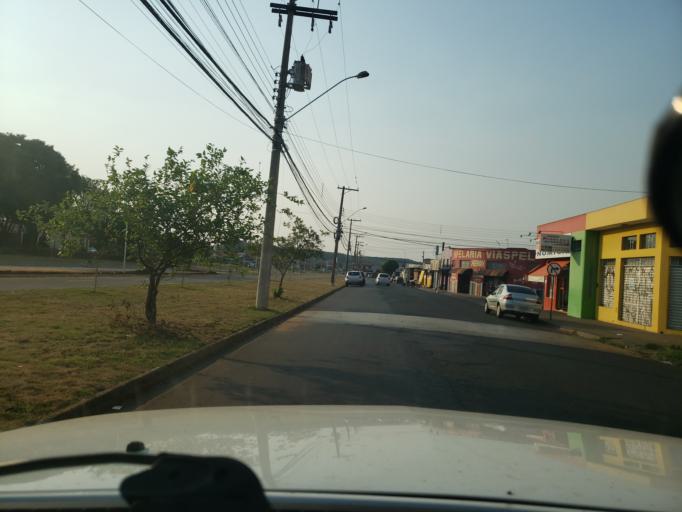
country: BR
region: Sao Paulo
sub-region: Moji-Guacu
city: Mogi-Gaucu
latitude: -22.3335
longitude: -46.9465
